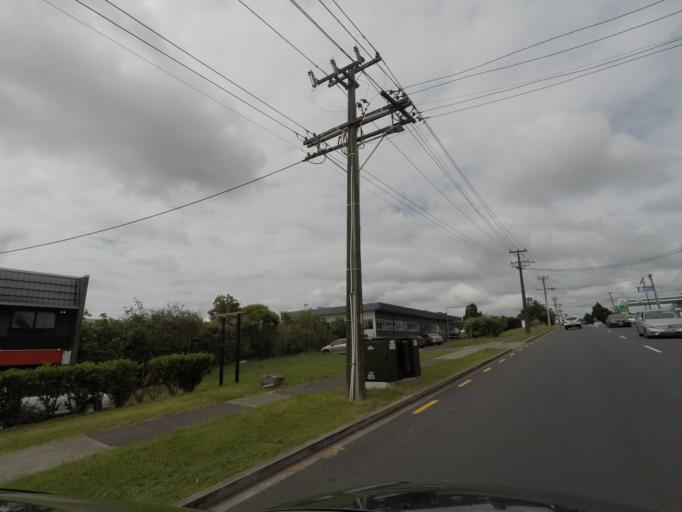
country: NZ
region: Auckland
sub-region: Auckland
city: Waitakere
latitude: -36.8928
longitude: 174.6298
